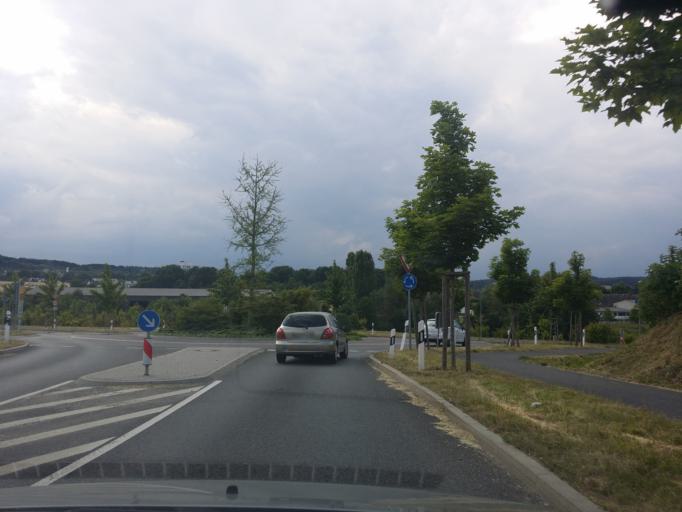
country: DE
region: Hesse
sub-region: Regierungsbezirk Darmstadt
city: Idstein
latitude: 50.2096
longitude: 8.2719
